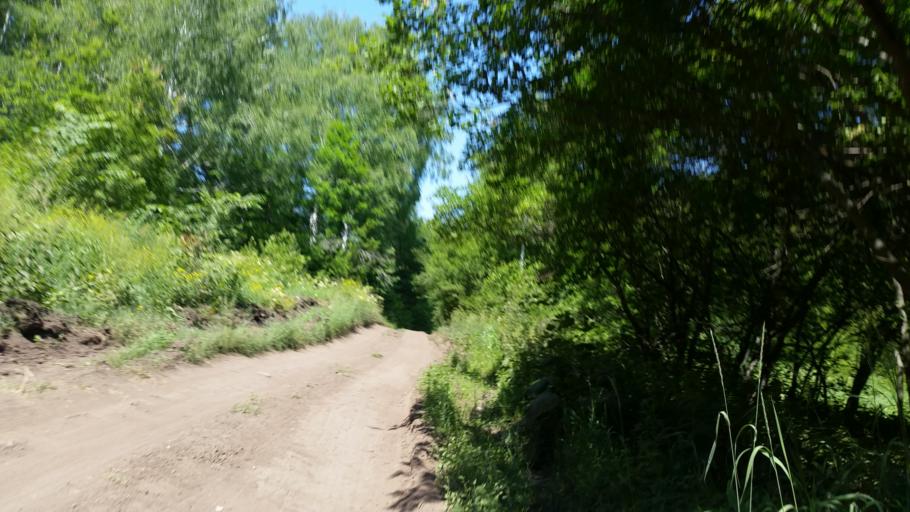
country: RU
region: Samara
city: Bogatyr'
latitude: 53.3983
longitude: 49.9333
